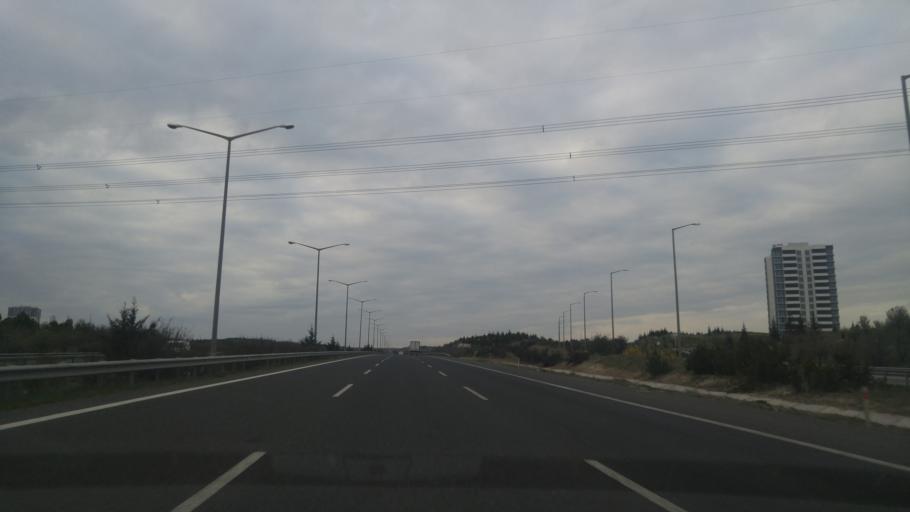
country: TR
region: Ankara
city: Etimesgut
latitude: 40.0078
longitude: 32.6318
